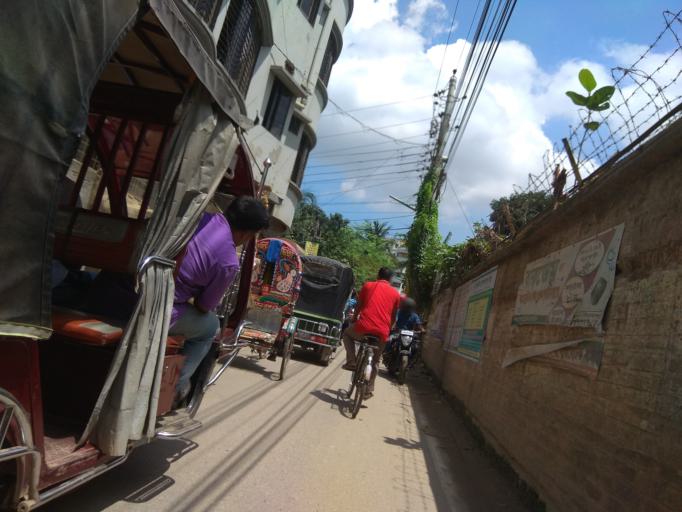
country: BD
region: Dhaka
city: Tungi
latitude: 23.8311
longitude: 90.3898
